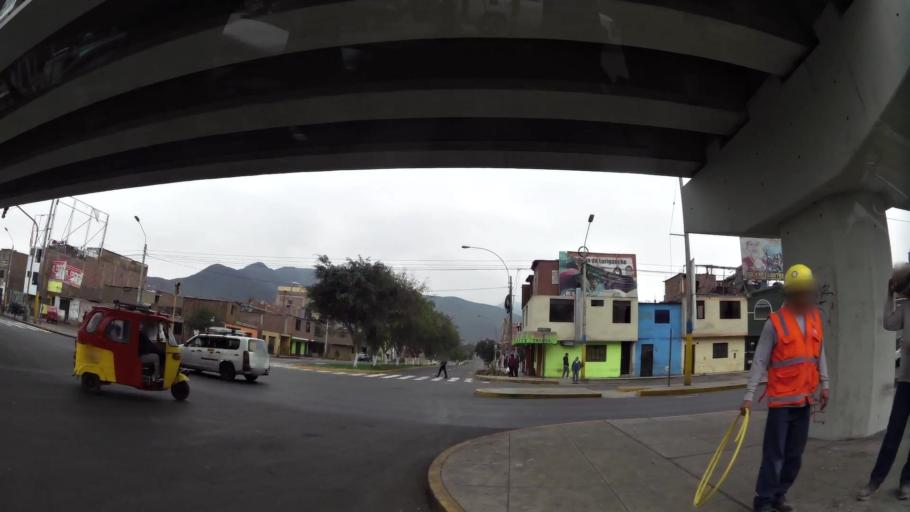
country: PE
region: Lima
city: Lima
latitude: -12.0228
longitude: -77.0088
